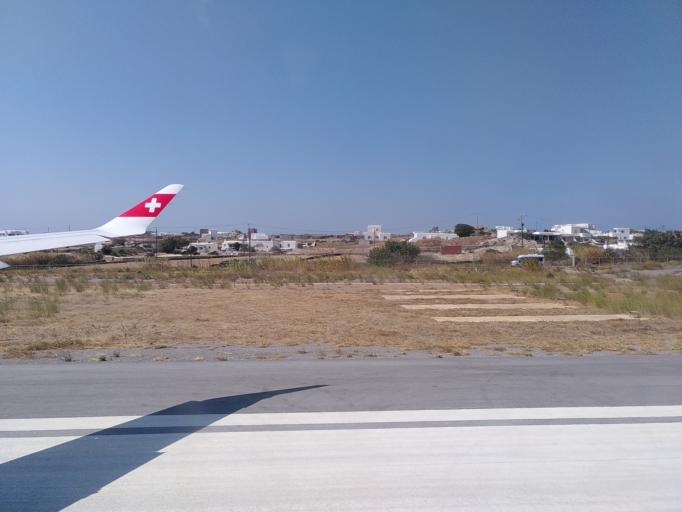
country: GR
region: South Aegean
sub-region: Nomos Kykladon
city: Mykonos
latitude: 37.4298
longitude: 25.3506
